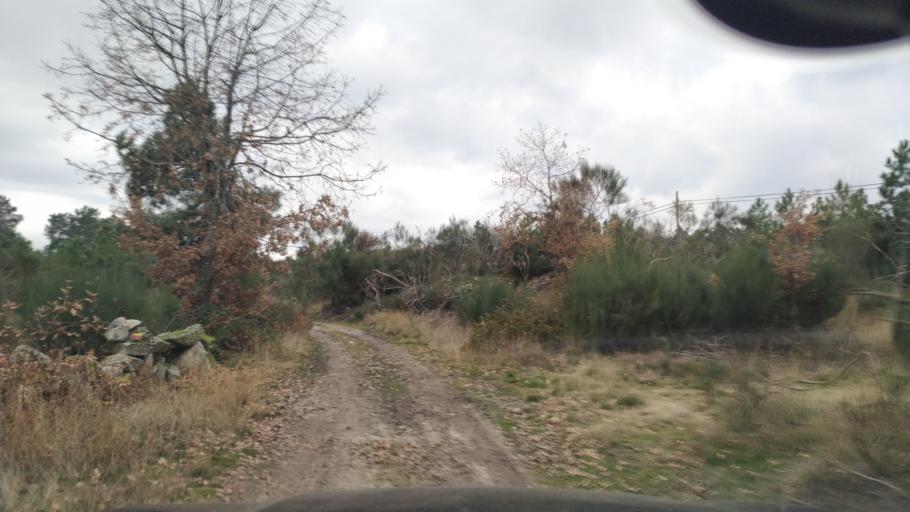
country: PT
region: Vila Real
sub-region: Sabrosa
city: Sabrosa
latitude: 41.3360
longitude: -7.6300
